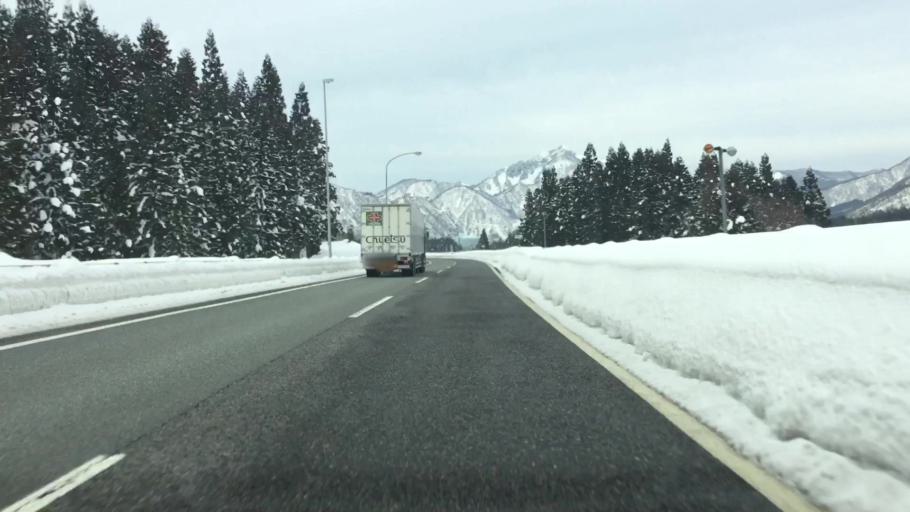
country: JP
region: Niigata
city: Shiozawa
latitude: 36.8888
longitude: 138.8484
